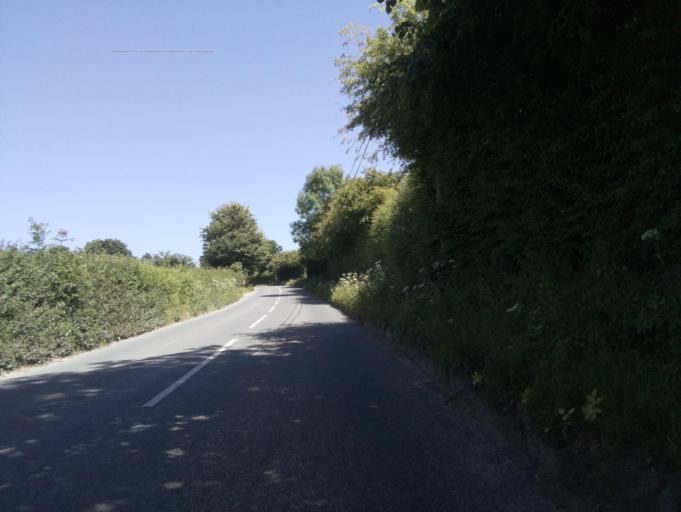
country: GB
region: England
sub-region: Devon
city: Kingskerswell
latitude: 50.4980
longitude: -3.5962
